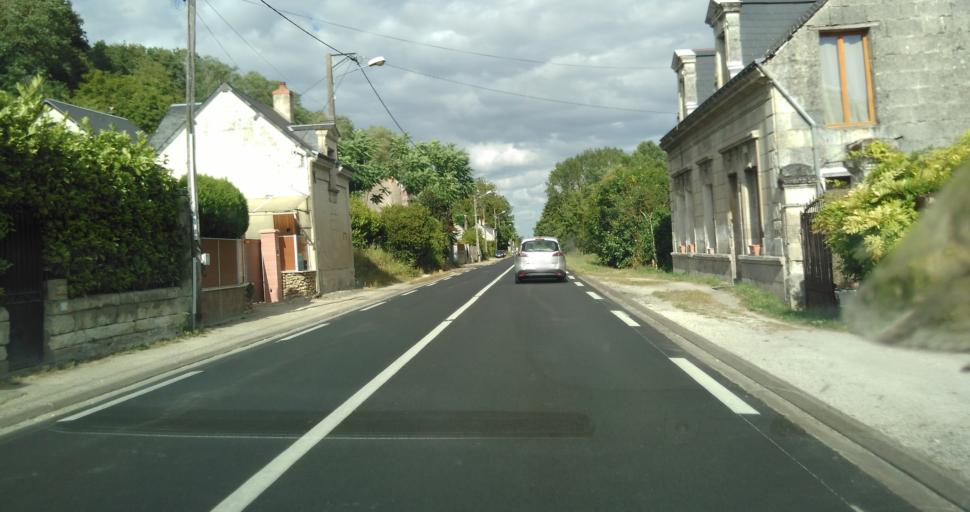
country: FR
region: Centre
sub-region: Departement d'Indre-et-Loire
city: Langeais
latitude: 47.3132
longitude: 0.3739
